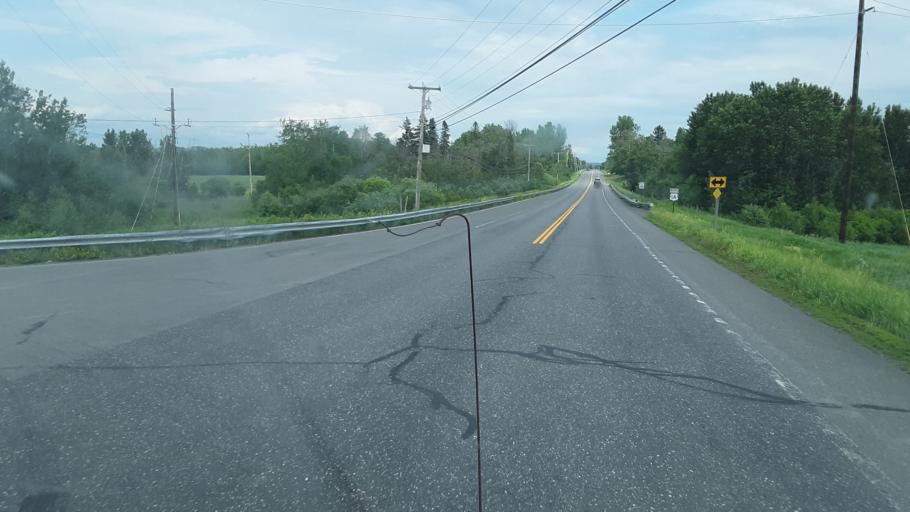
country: US
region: Maine
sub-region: Aroostook County
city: Fort Fairfield
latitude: 46.7602
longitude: -67.8586
